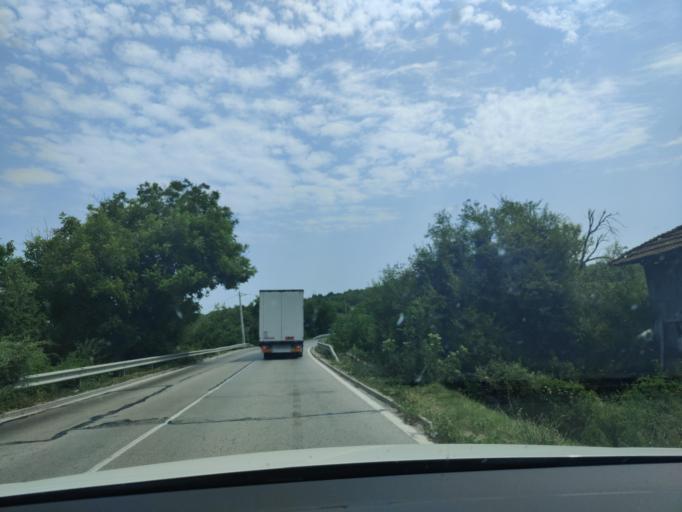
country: BG
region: Vidin
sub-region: Obshtina Ruzhintsi
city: Ruzhintsi
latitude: 43.6555
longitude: 22.7879
